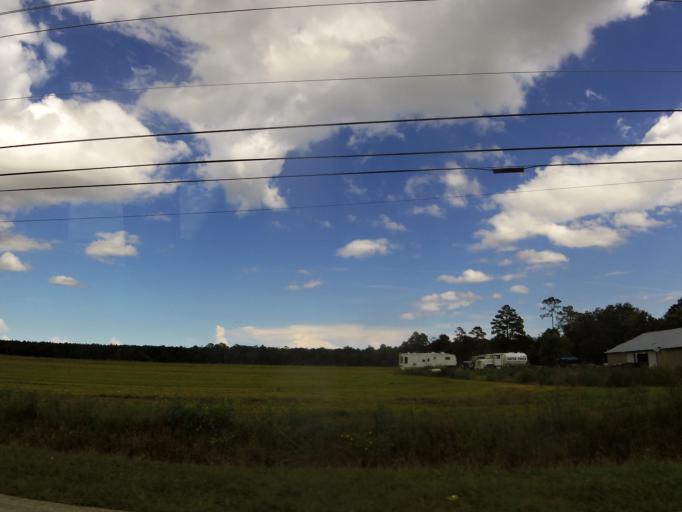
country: US
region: Florida
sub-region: Saint Johns County
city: Saint Augustine South
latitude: 29.8429
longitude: -81.4994
